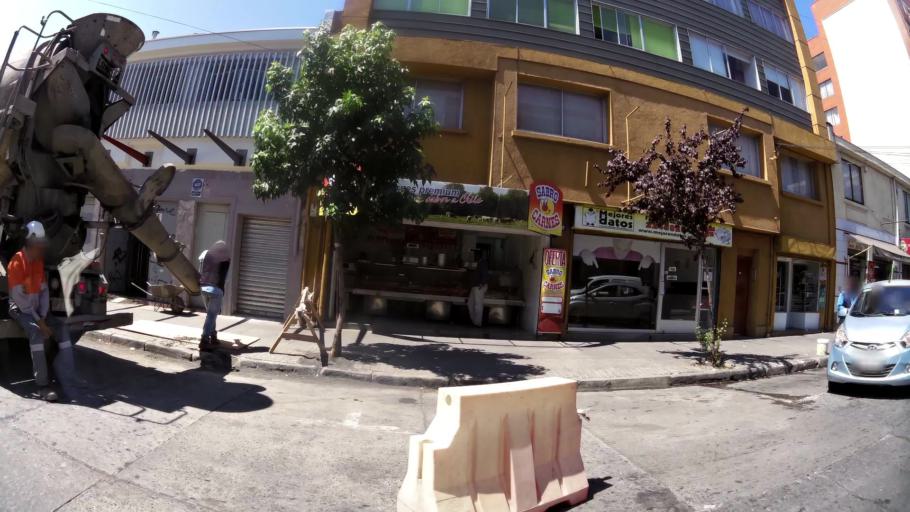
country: CL
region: Biobio
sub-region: Provincia de Concepcion
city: Concepcion
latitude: -36.8240
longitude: -73.0498
